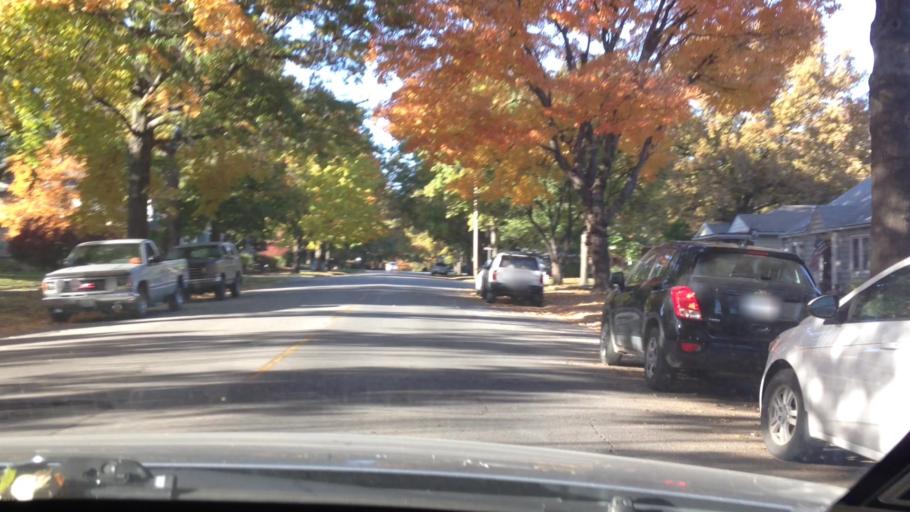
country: US
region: Kansas
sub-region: Leavenworth County
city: Leavenworth
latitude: 39.3210
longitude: -94.9220
